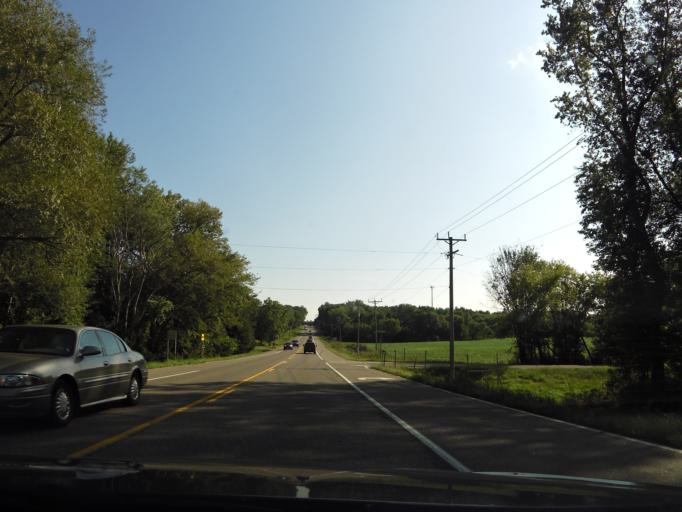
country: US
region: Minnesota
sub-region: Washington County
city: Lake Elmo
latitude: 44.9342
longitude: -92.8627
